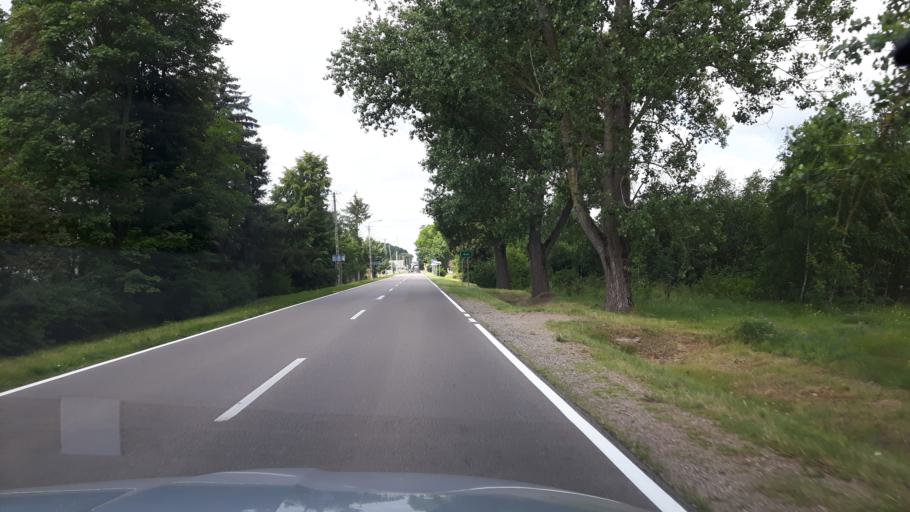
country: PL
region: Masovian Voivodeship
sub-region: Powiat ostrowski
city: Brok
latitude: 52.7040
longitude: 21.8963
